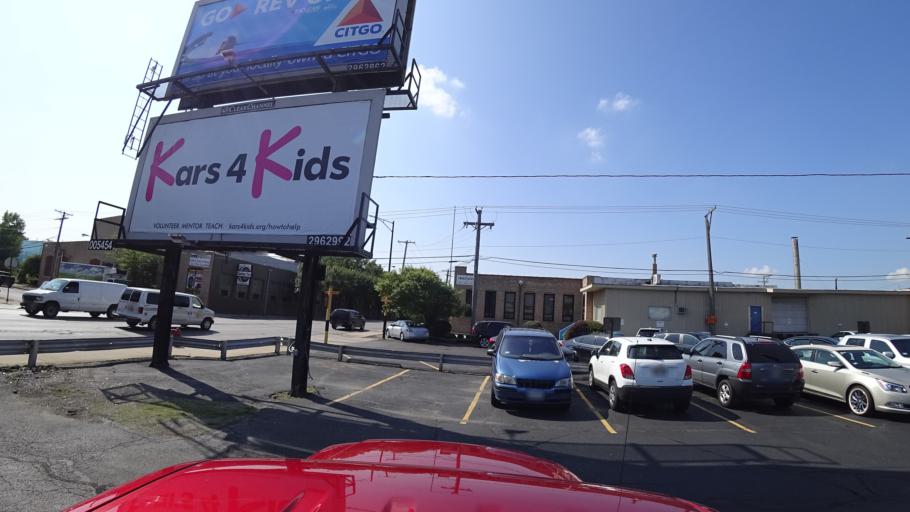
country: US
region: Illinois
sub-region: Cook County
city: Cicero
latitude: 41.8274
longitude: -87.7048
